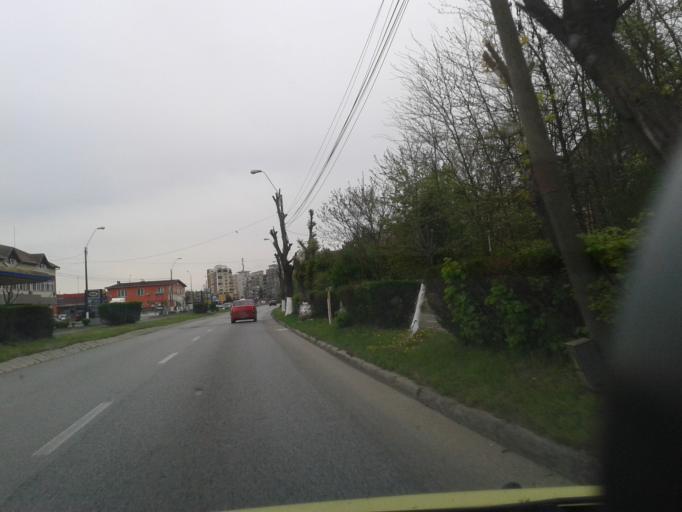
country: RO
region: Hunedoara
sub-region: Municipiul Deva
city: Deva
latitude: 45.8875
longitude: 22.9072
